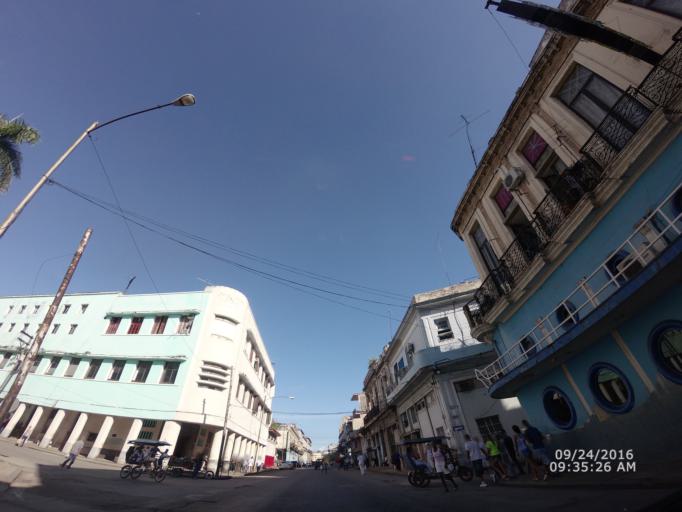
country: CU
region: La Habana
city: La Habana Vieja
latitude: 23.1318
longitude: -82.3552
